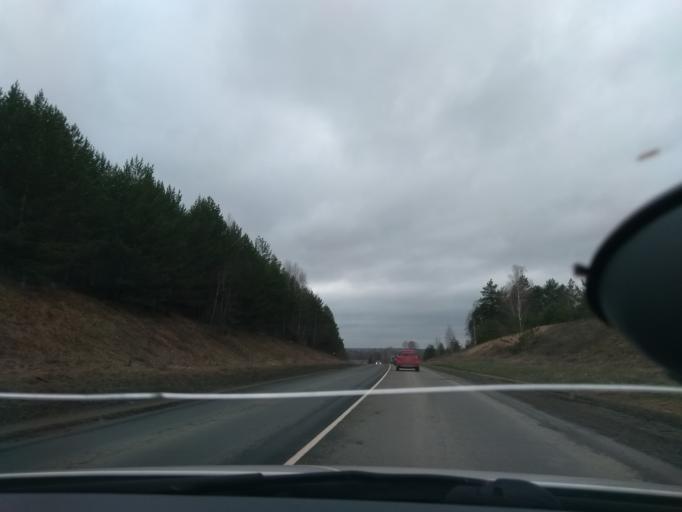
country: RU
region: Perm
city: Kungur
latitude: 57.4821
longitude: 56.7005
